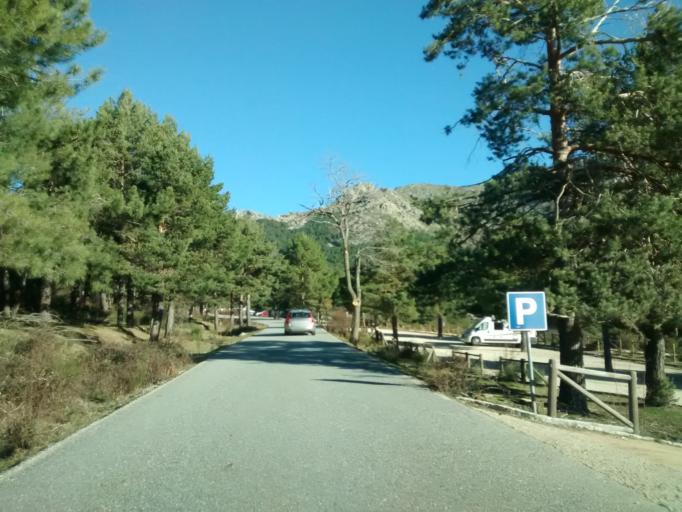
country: ES
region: Madrid
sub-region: Provincia de Madrid
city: Navacerrada
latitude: 40.7498
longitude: -3.9936
